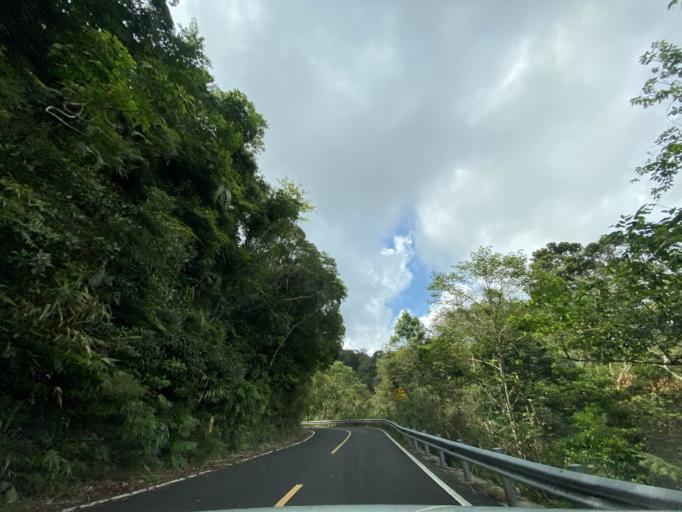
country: CN
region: Hainan
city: Diaoluoshan
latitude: 18.7132
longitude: 109.8806
